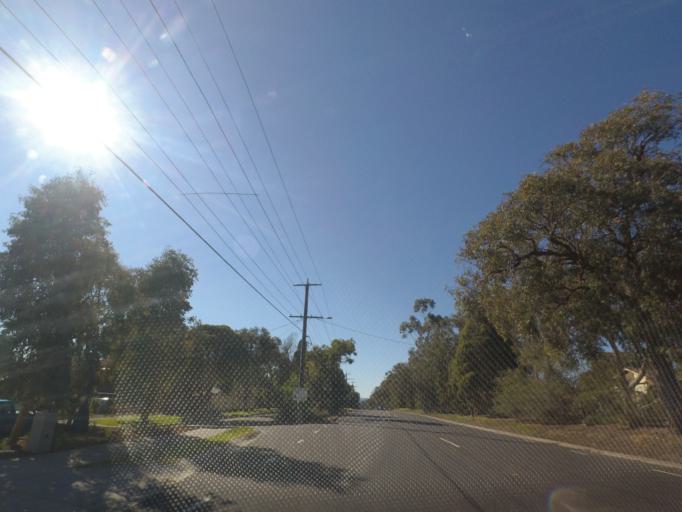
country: AU
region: Victoria
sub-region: Maroondah
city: Croydon Hills
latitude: -37.7782
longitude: 145.2748
